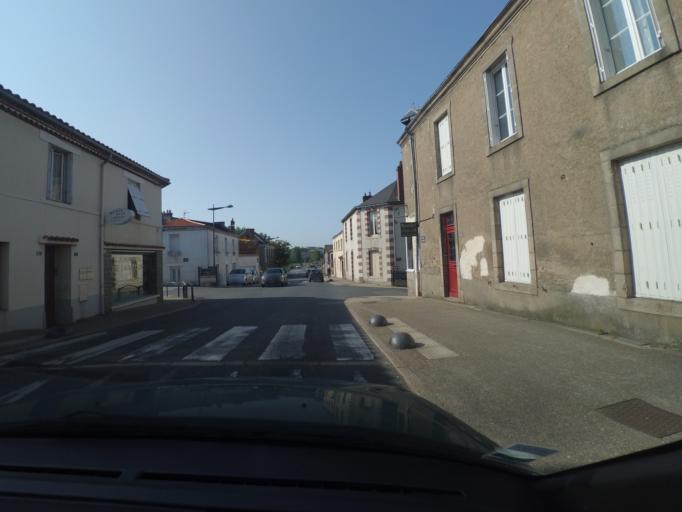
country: FR
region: Pays de la Loire
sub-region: Departement de la Loire-Atlantique
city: Mouzillon
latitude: 47.1408
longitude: -1.2825
